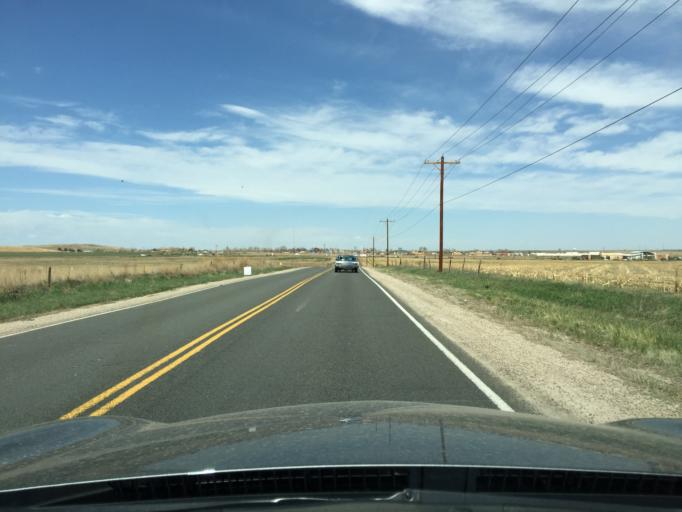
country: US
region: Colorado
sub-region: Boulder County
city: Erie
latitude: 39.9943
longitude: -104.9972
